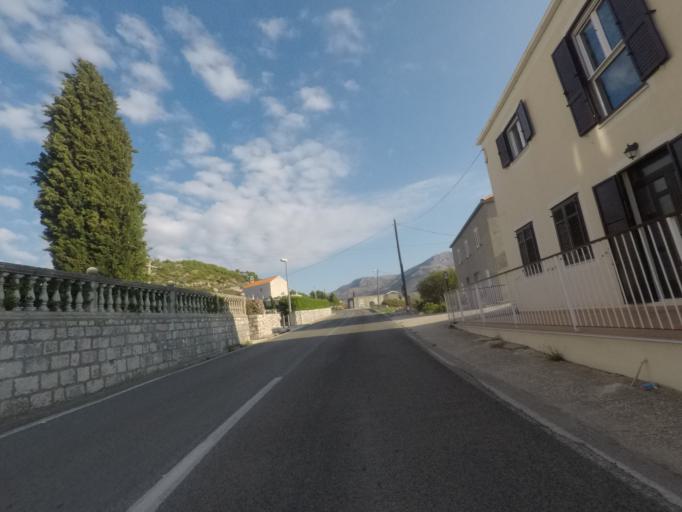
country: HR
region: Dubrovacko-Neretvanska
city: Cibaca
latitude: 42.6443
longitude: 18.1584
